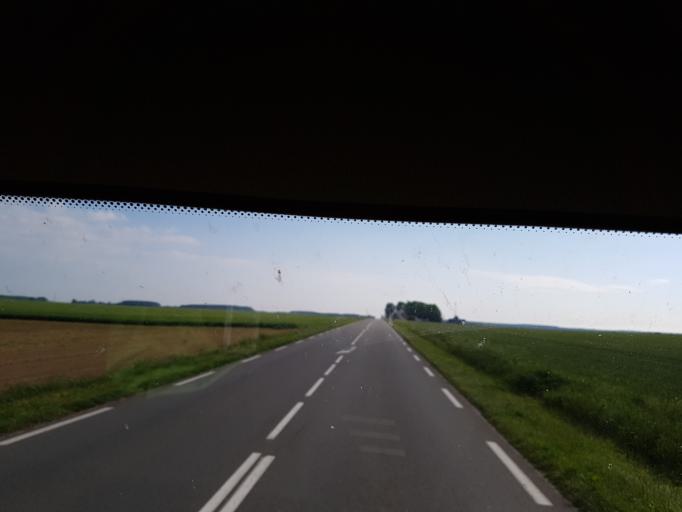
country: FR
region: Picardie
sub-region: Departement de la Somme
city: Crecy-en-Ponthieu
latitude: 50.2468
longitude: 1.9598
